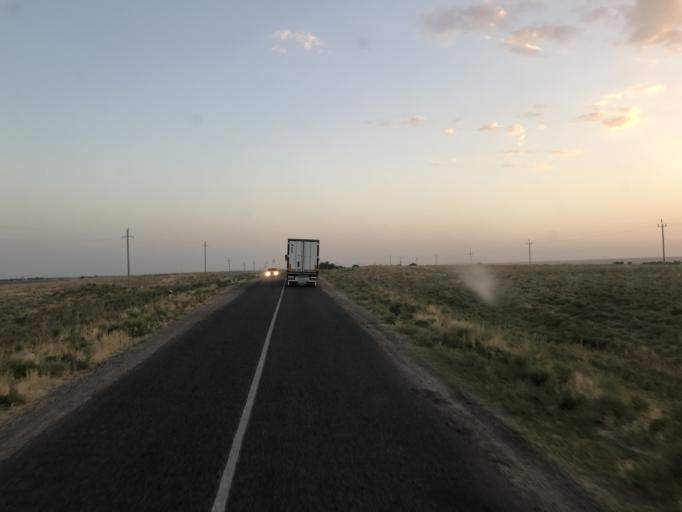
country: UZ
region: Toshkent
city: Amir Timur
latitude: 41.3344
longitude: 68.6887
